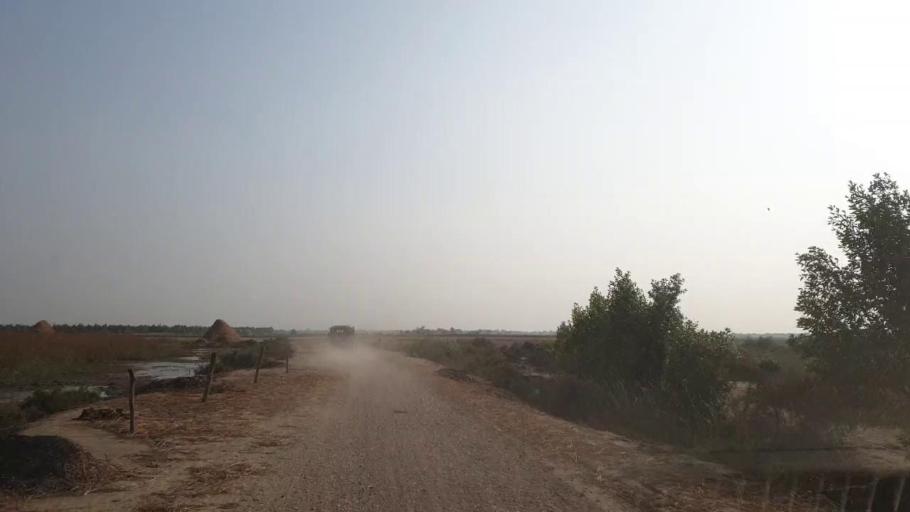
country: PK
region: Sindh
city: Kario
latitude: 24.9141
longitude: 68.5685
